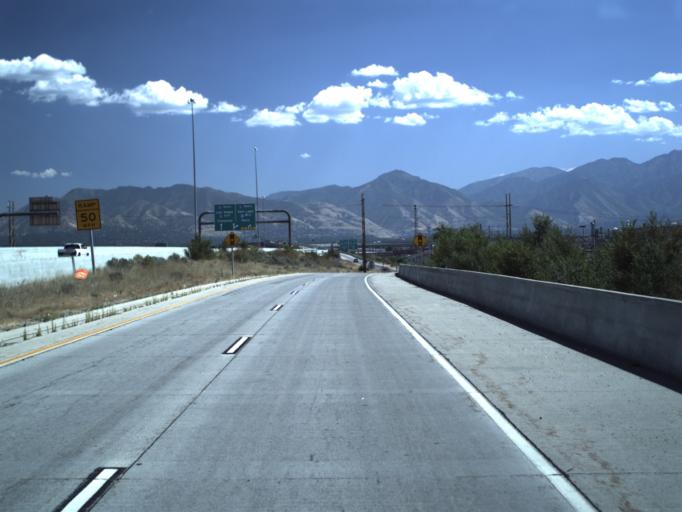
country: US
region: Utah
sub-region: Salt Lake County
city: South Salt Lake
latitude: 40.7241
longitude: -111.9214
